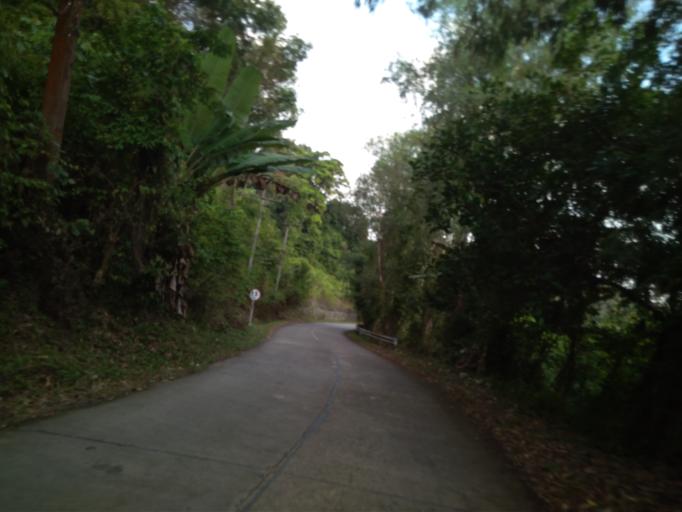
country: TH
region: Phangnga
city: Ko Yao
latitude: 8.1376
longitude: 98.6176
